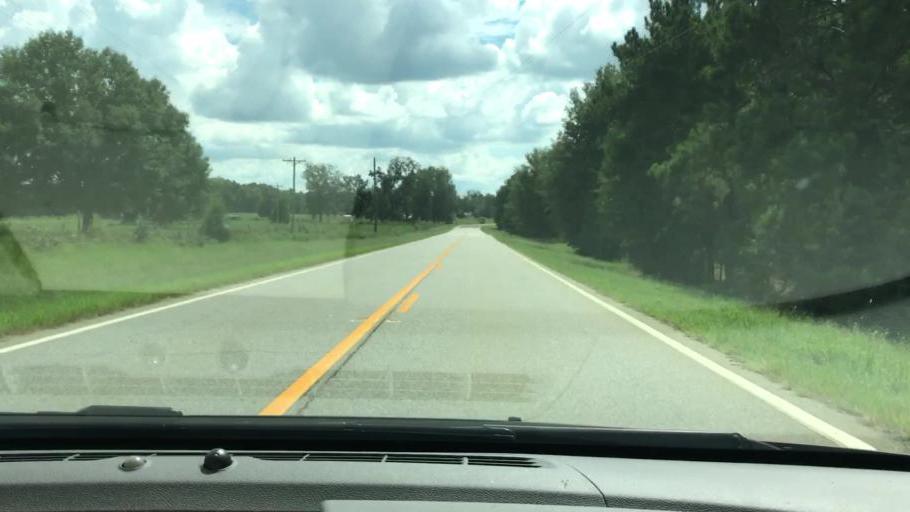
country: US
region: Georgia
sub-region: Quitman County
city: Georgetown
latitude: 31.8985
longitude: -85.0802
